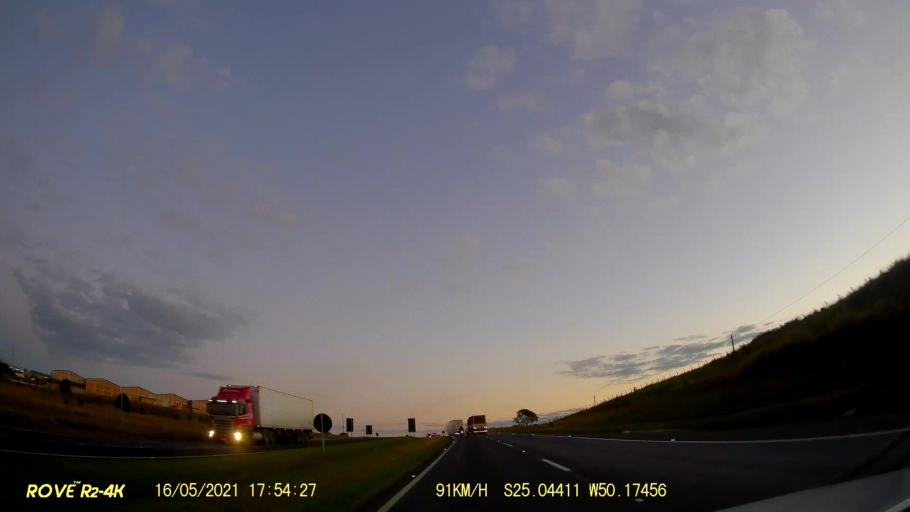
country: BR
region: Parana
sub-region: Ponta Grossa
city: Ponta Grossa
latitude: -25.0442
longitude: -50.1744
